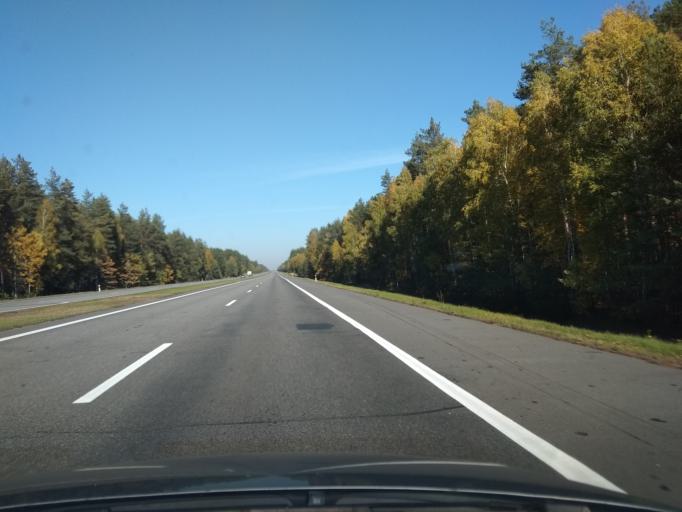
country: BY
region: Grodnenskaya
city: Zhyrovichy
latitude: 52.8697
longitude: 25.6572
